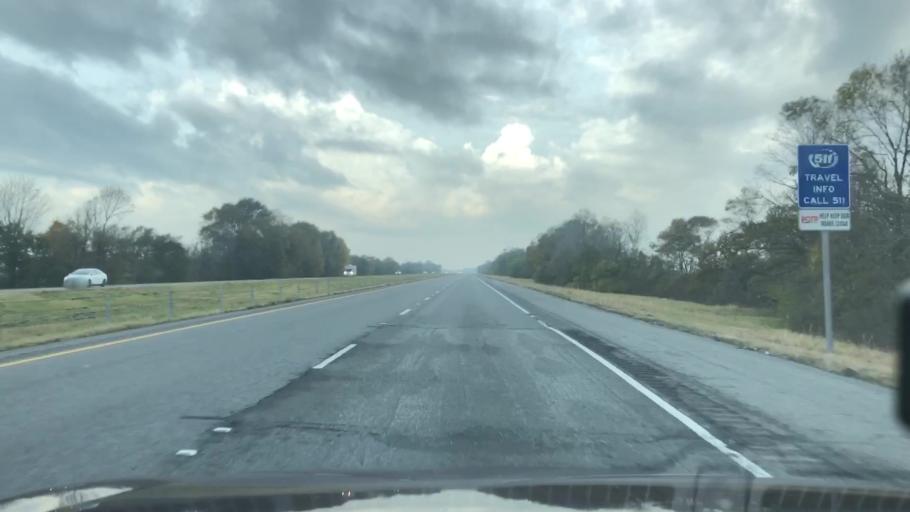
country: US
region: Louisiana
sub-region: Madison Parish
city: Tallulah
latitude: 32.4108
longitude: -91.2544
